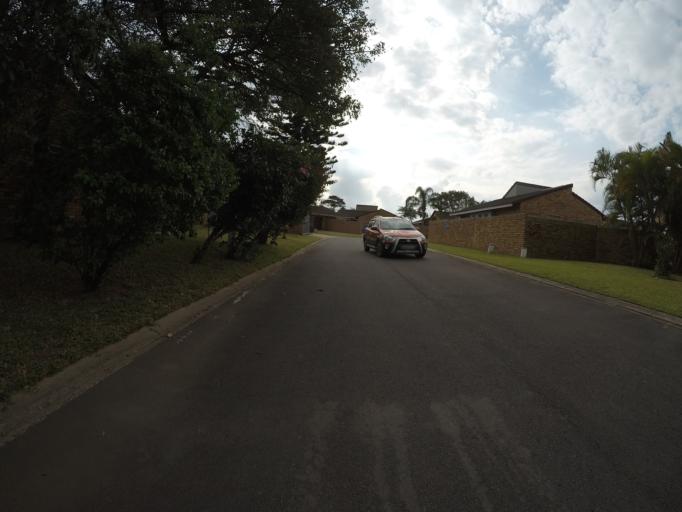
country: ZA
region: KwaZulu-Natal
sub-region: uThungulu District Municipality
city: Richards Bay
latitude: -28.7377
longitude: 32.0837
